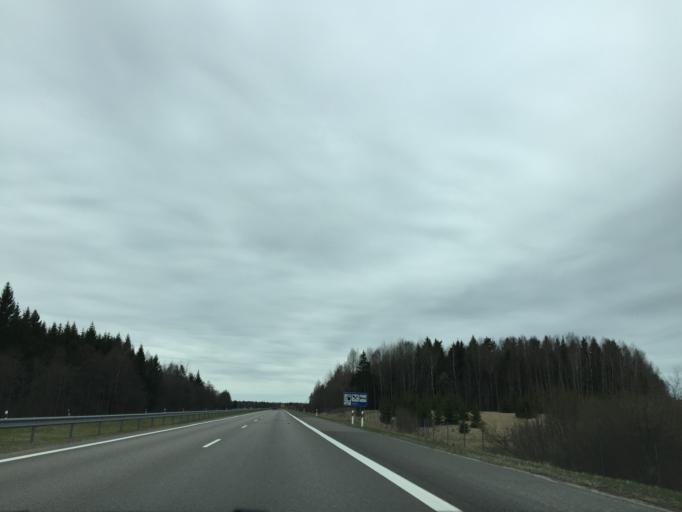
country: LT
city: Rietavas
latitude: 55.6803
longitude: 21.7051
